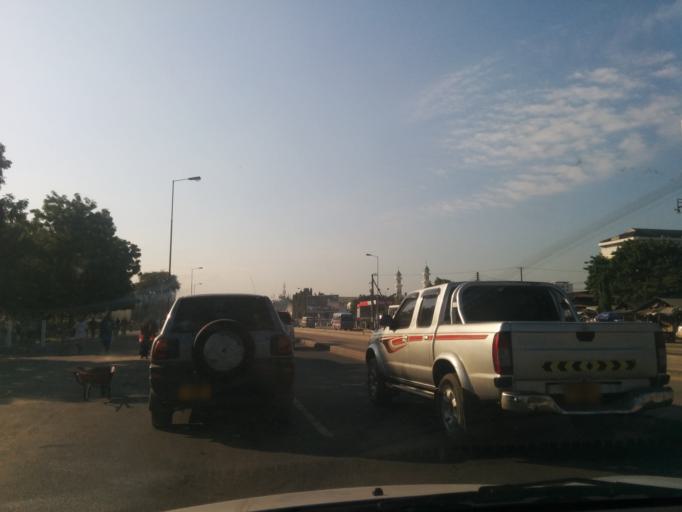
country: TZ
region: Dar es Salaam
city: Magomeni
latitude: -6.8067
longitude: 39.2562
